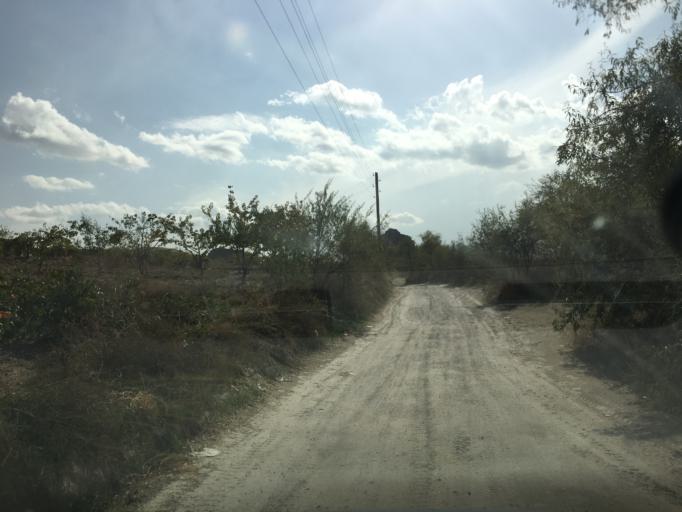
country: TR
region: Nevsehir
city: Goereme
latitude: 38.6643
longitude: 34.8413
